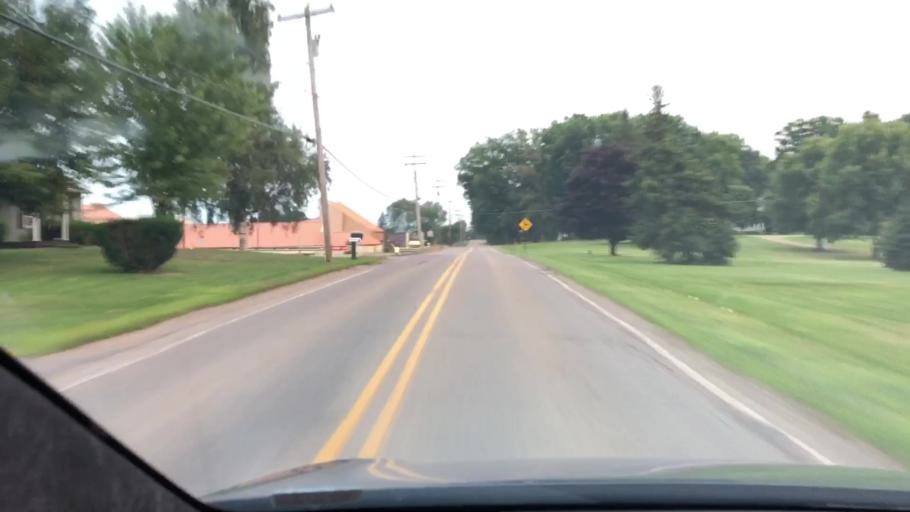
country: US
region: Pennsylvania
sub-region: Butler County
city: Shanor-Northvue
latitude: 40.8946
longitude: -79.9281
